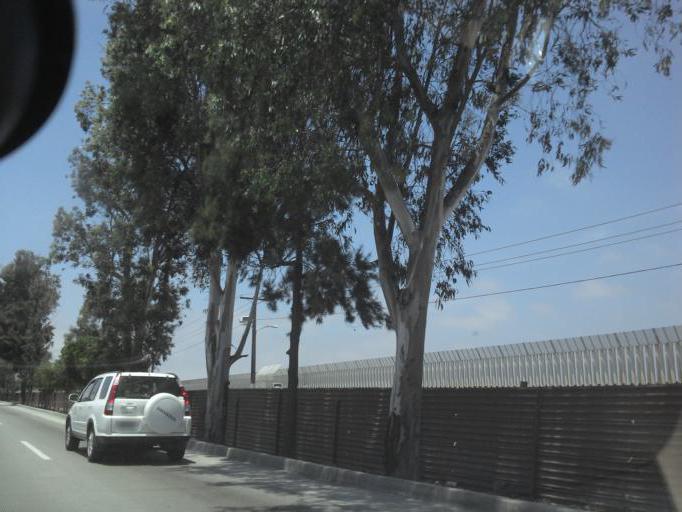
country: MX
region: Baja California
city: Tijuana
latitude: 32.5405
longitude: -117.0514
